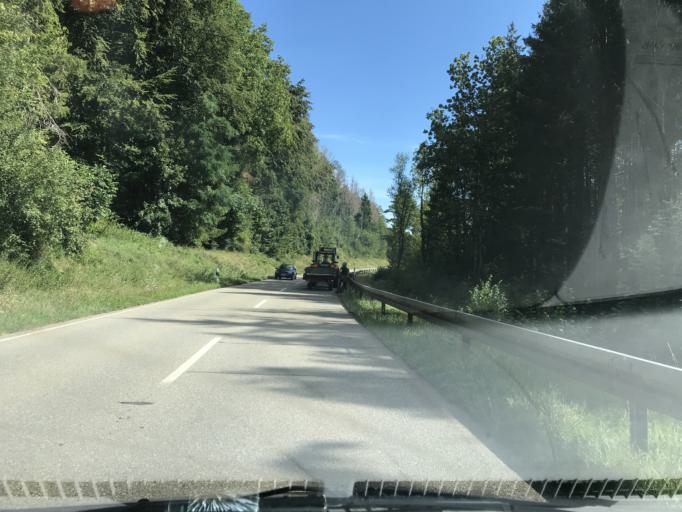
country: DE
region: Baden-Wuerttemberg
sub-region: Freiburg Region
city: Schworstadt
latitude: 47.6121
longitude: 7.8639
